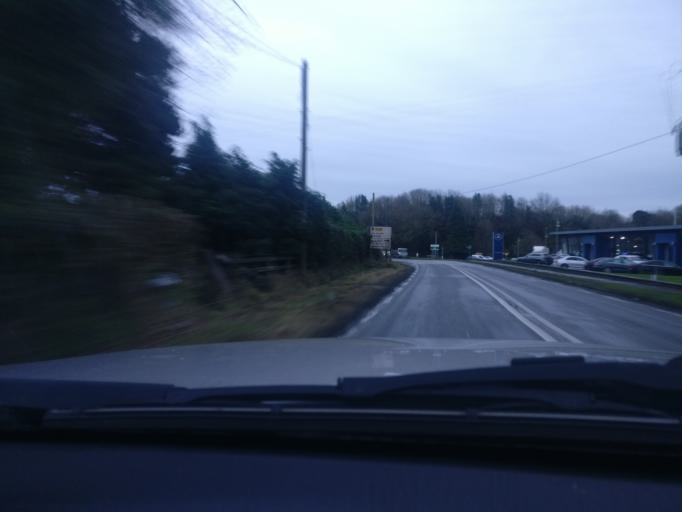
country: IE
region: Leinster
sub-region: An Mhi
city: Navan
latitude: 53.6604
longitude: -6.7234
